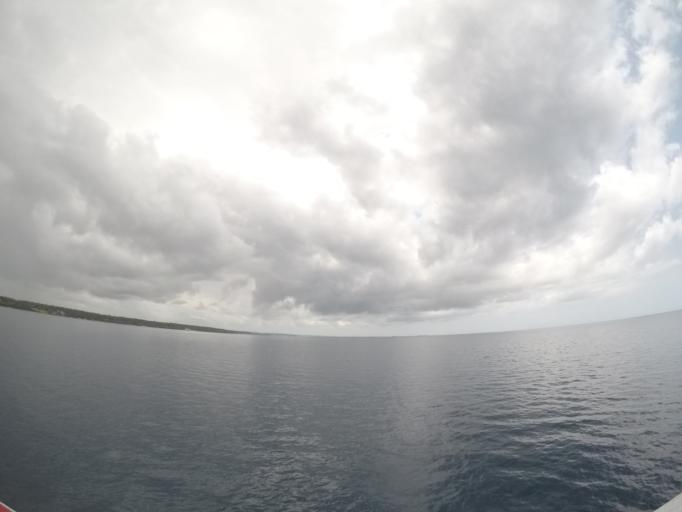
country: TZ
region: Zanzibar North
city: Mkokotoni
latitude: -5.9757
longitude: 39.1716
